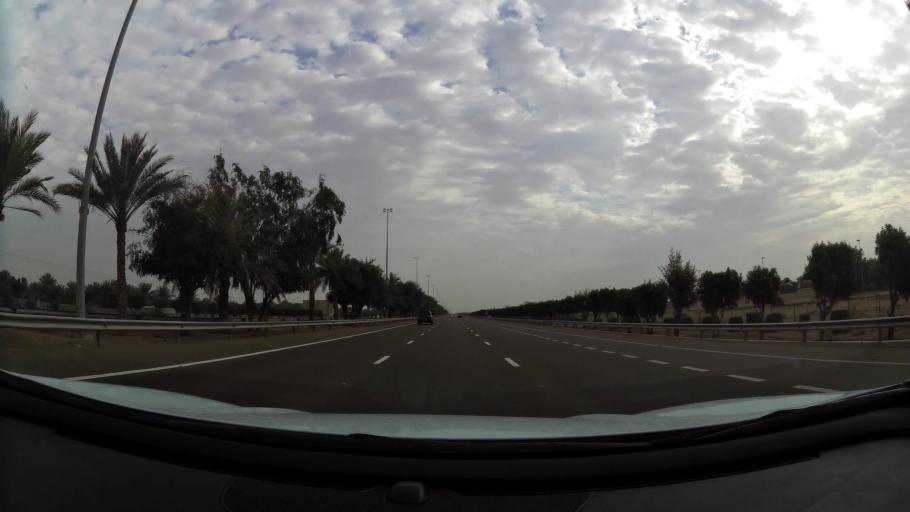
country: AE
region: Abu Dhabi
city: Al Ain
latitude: 24.1916
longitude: 55.3530
